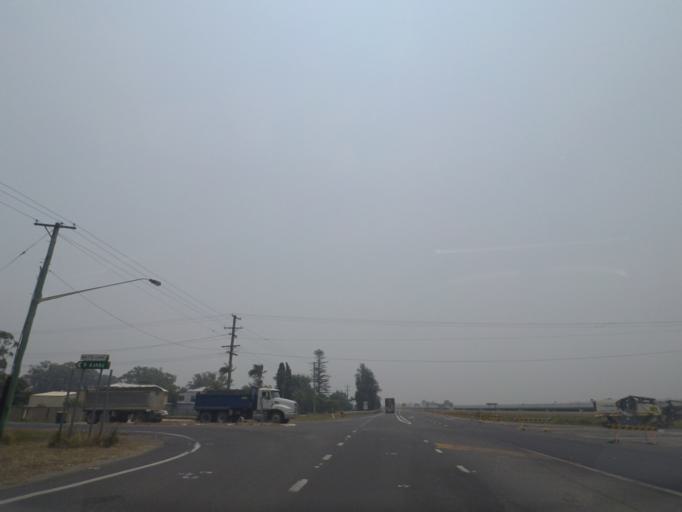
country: AU
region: New South Wales
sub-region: Clarence Valley
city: Maclean
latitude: -29.4191
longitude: 153.2407
